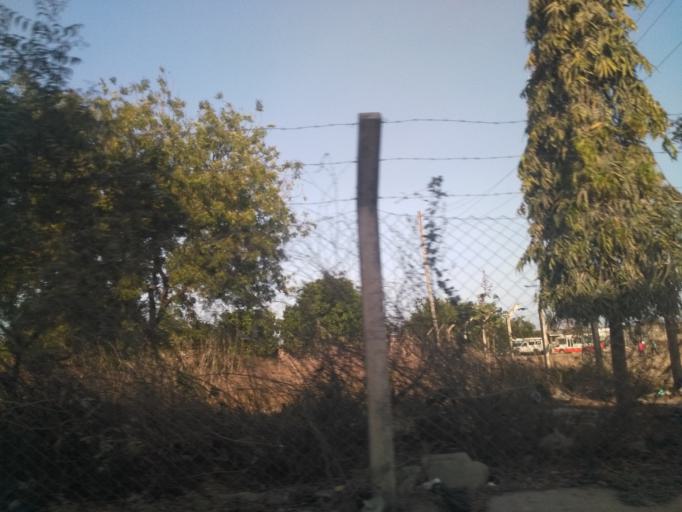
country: TZ
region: Pwani
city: Vikindu
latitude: -6.9214
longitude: 39.2679
